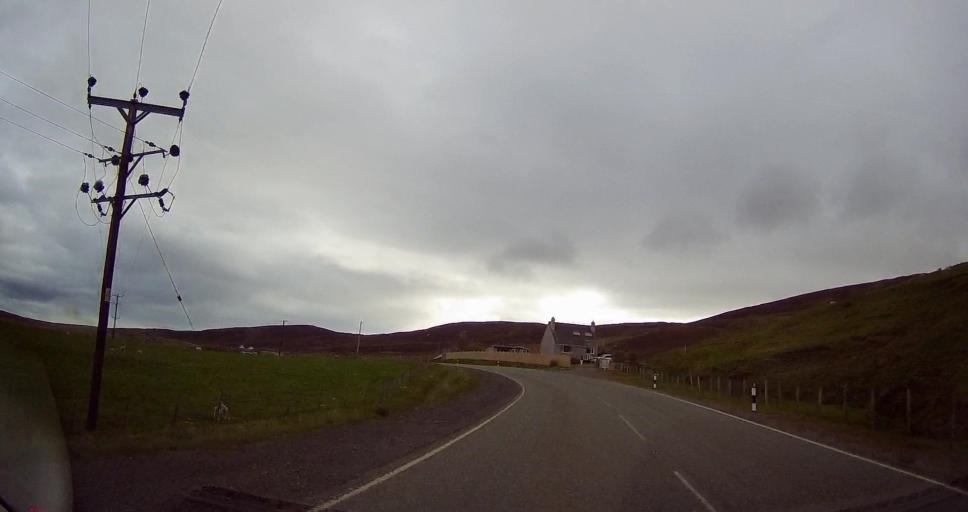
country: GB
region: Scotland
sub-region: Shetland Islands
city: Lerwick
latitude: 60.4120
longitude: -1.3257
